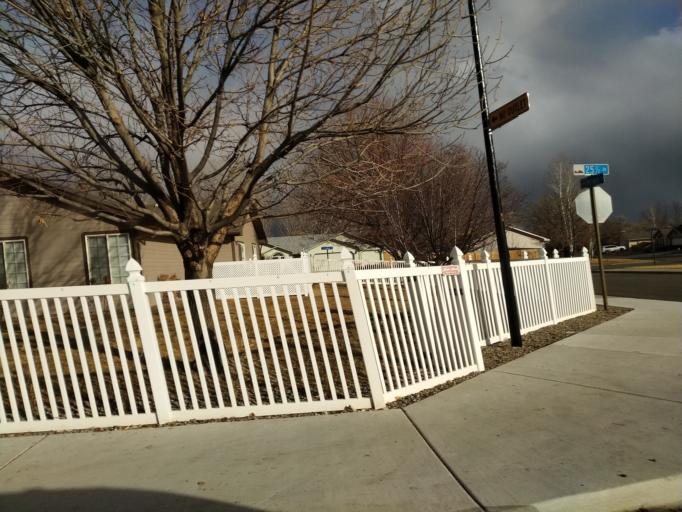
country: US
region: Colorado
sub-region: Mesa County
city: Grand Junction
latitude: 39.1015
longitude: -108.5801
